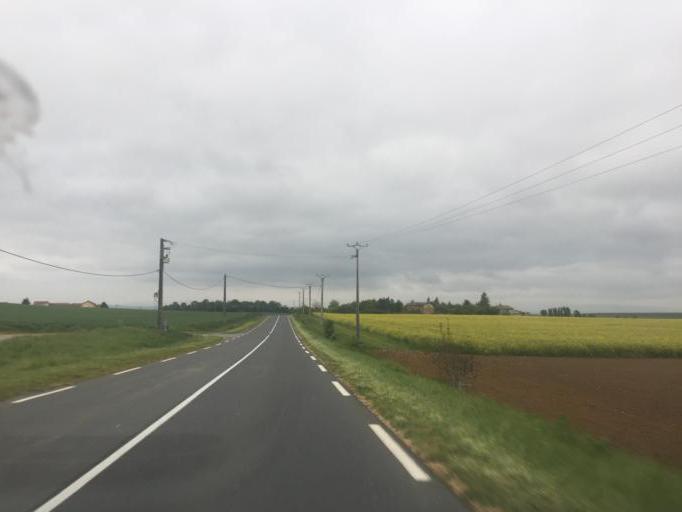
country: FR
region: Rhone-Alpes
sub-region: Departement de l'Ain
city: Civrieux
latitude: 45.9383
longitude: 4.8660
